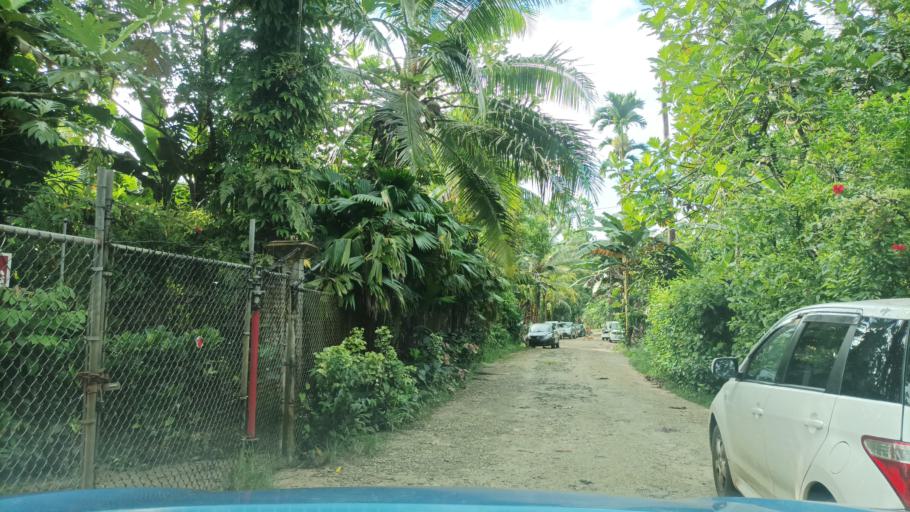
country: FM
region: Pohnpei
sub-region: Sokehs Municipality
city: Palikir - National Government Center
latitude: 6.9014
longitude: 158.1561
